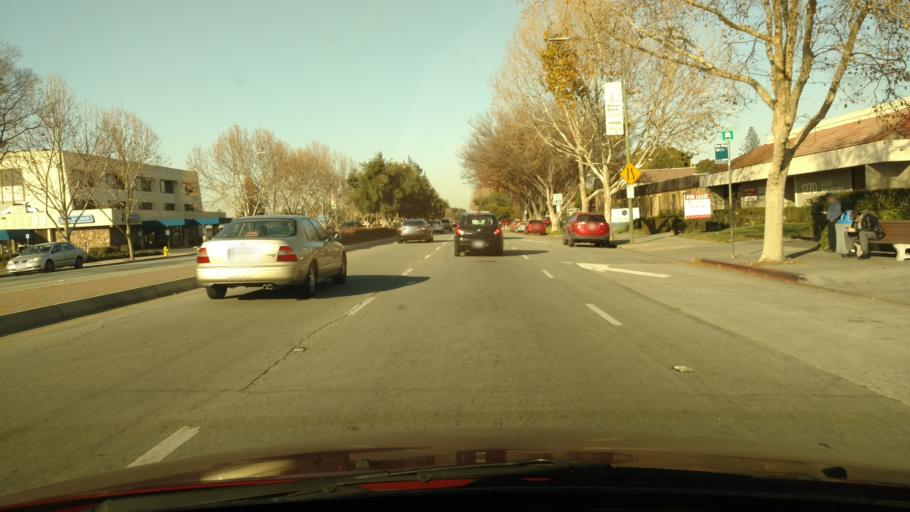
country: US
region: California
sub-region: Santa Clara County
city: Campbell
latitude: 37.3018
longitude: -121.9499
